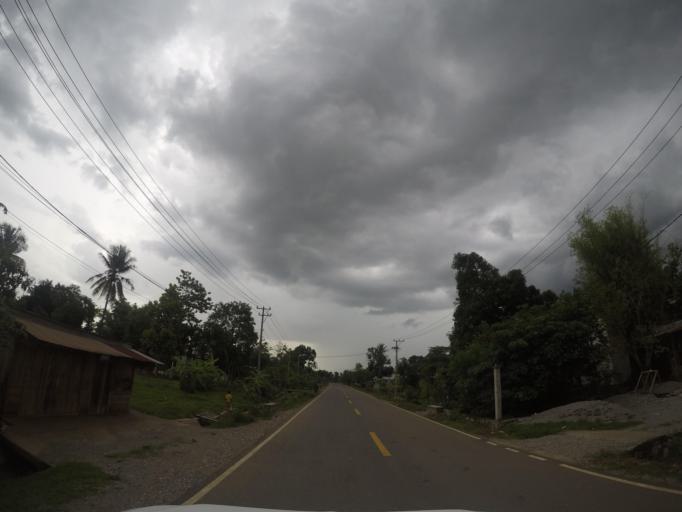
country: TL
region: Bobonaro
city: Maliana
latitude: -8.9706
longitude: 125.2186
